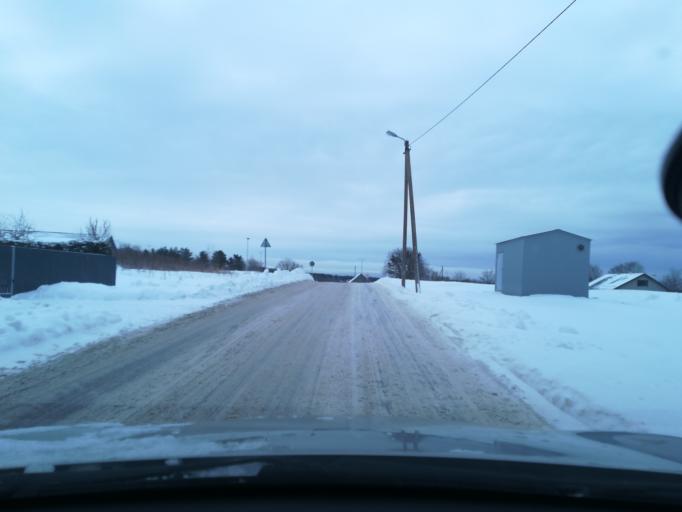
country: EE
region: Harju
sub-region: Harku vald
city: Tabasalu
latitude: 59.4434
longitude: 24.4928
